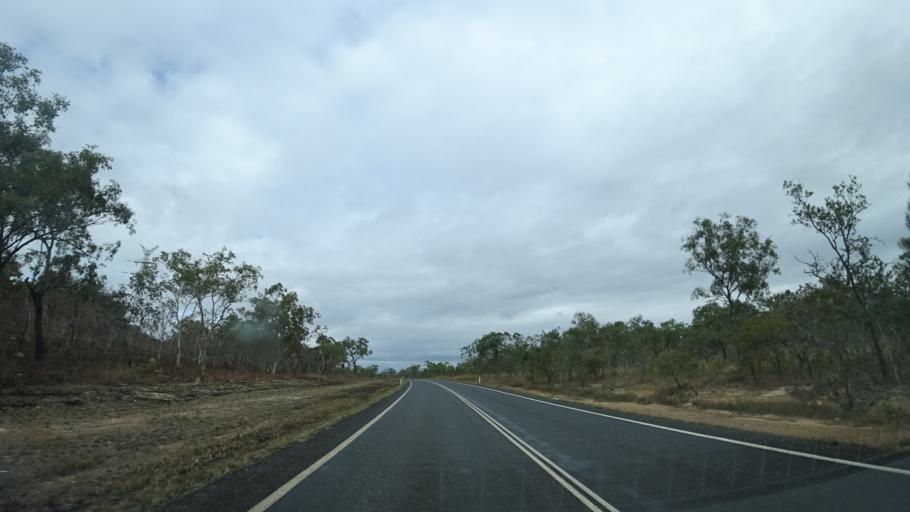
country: AU
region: Queensland
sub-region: Tablelands
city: Mareeba
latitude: -16.7755
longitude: 145.3402
